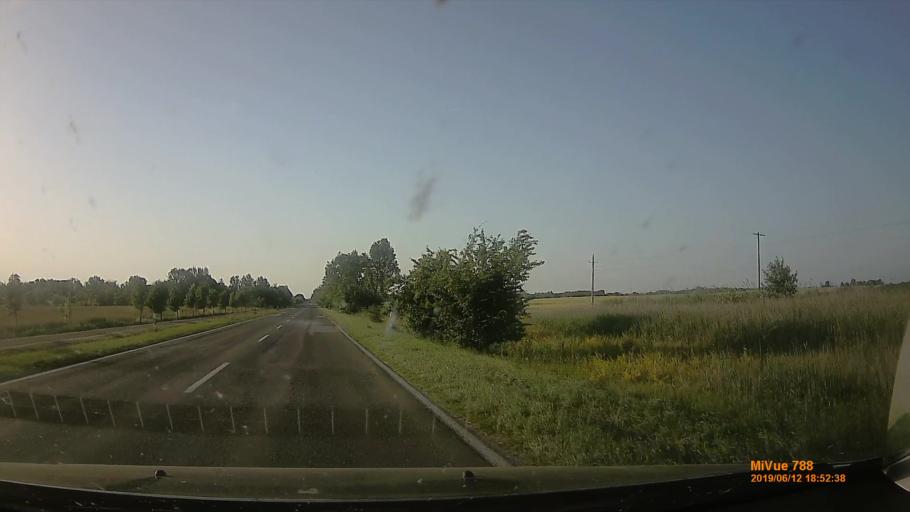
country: HU
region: Bacs-Kiskun
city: Kiskunfelegyhaza
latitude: 46.6783
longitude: 19.8536
